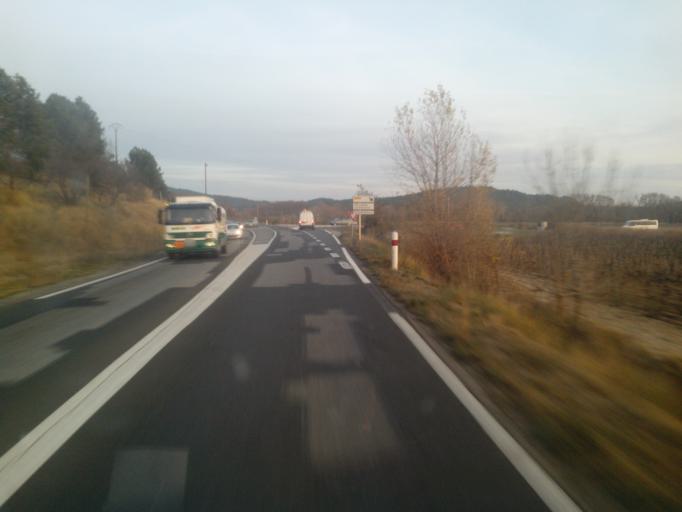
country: FR
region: Languedoc-Roussillon
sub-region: Departement de l'Herault
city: Olonzac
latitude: 43.2663
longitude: 2.7340
